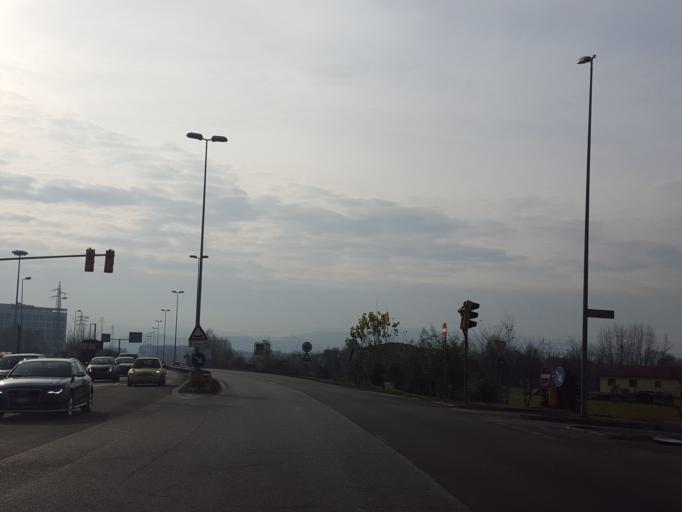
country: IT
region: Veneto
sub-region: Provincia di Vicenza
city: Creazzo
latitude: 45.5472
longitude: 11.5093
